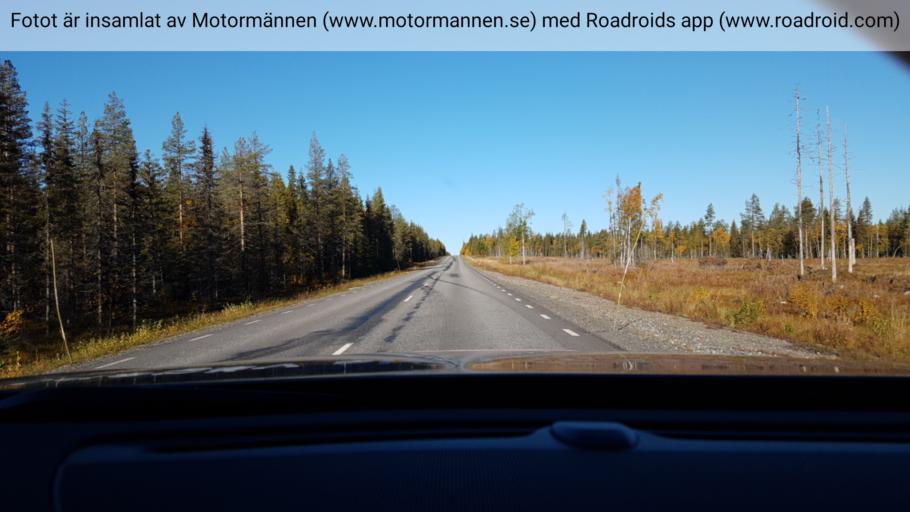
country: SE
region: Vaesterbotten
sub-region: Skelleftea Kommun
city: Storvik
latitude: 65.3515
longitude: 20.4908
